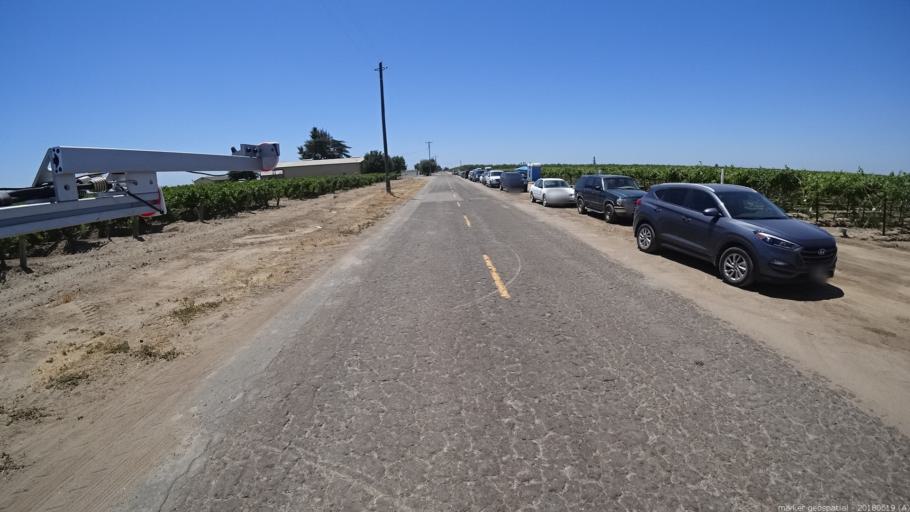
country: US
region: California
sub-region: Madera County
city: Parkwood
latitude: 36.8604
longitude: -120.0741
